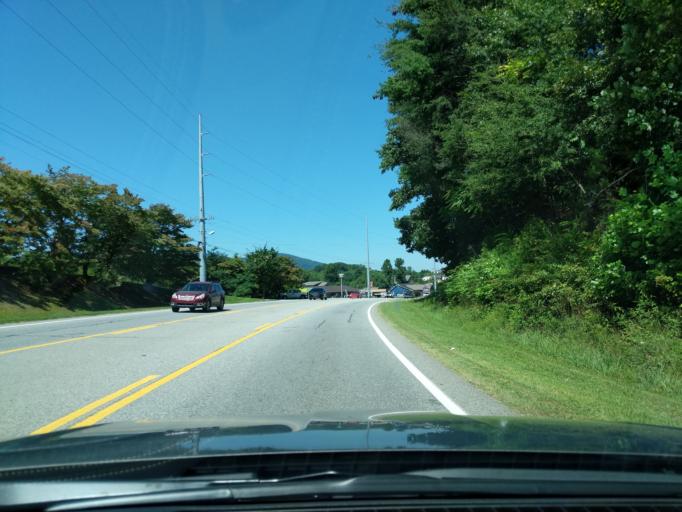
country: US
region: Georgia
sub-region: Towns County
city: Hiawassee
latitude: 34.9407
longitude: -83.7470
